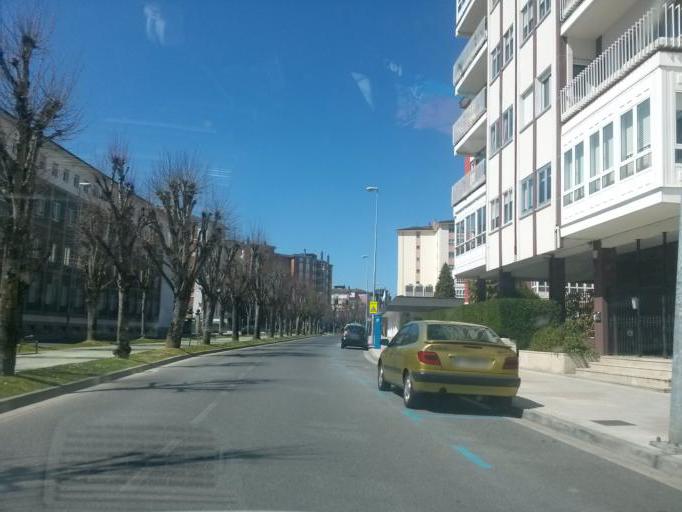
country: ES
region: Galicia
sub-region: Provincia de Lugo
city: Lugo
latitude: 43.0027
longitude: -7.5515
